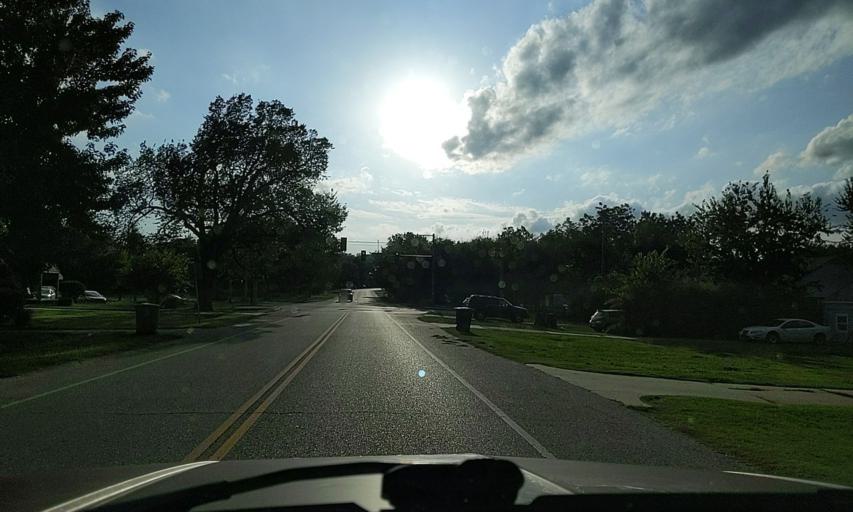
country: US
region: Oklahoma
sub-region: Tulsa County
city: Tulsa
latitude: 36.1933
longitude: -95.9859
